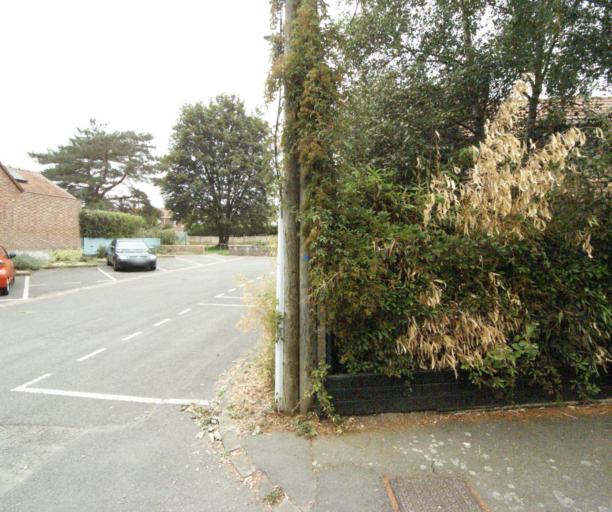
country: FR
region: Nord-Pas-de-Calais
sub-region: Departement du Nord
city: Mons-en-Baroeul
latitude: 50.6374
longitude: 3.1290
